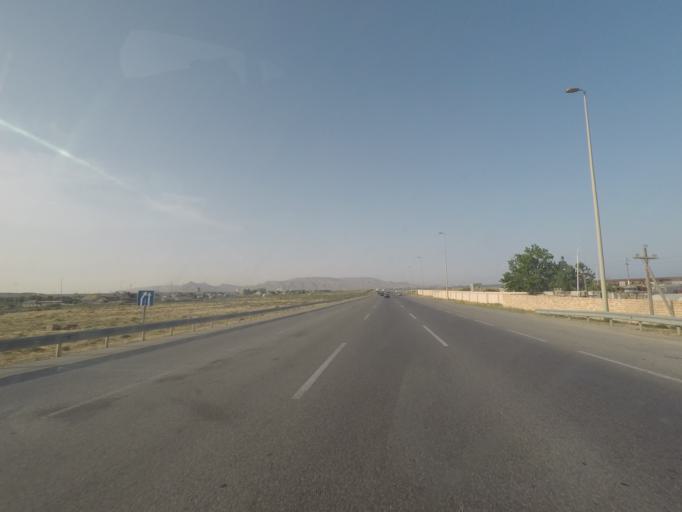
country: AZ
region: Baki
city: Qobustan
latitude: 40.1569
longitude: 49.4607
